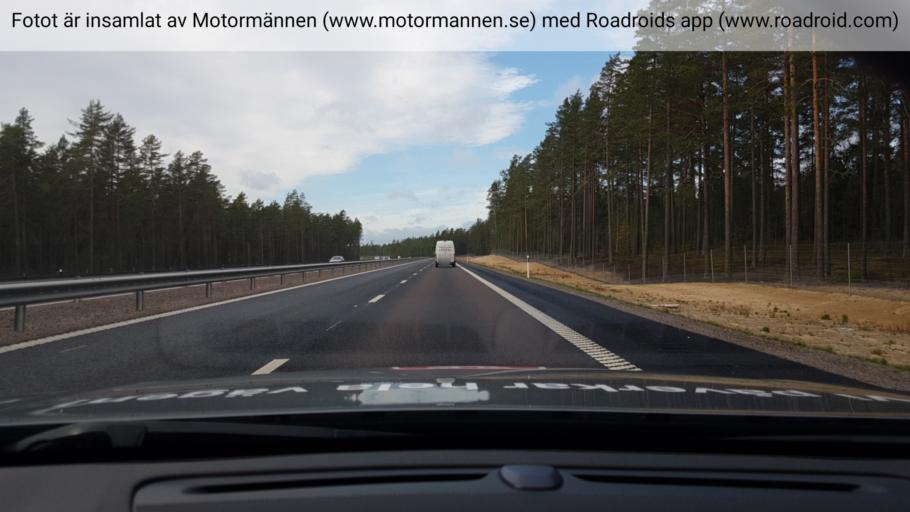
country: SE
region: Vaermland
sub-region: Kils Kommun
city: Kil
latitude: 59.3841
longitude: 13.3547
